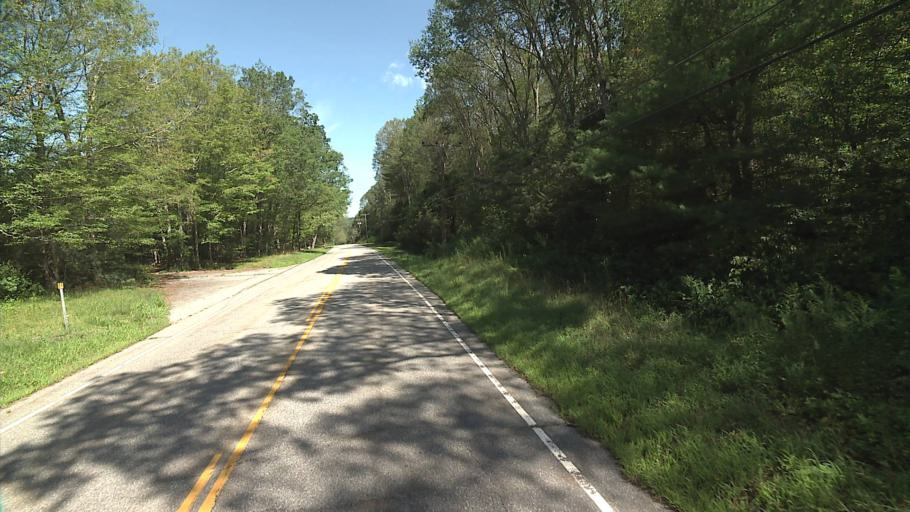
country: US
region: Connecticut
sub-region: New London County
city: Baltic
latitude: 41.6816
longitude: -72.0847
